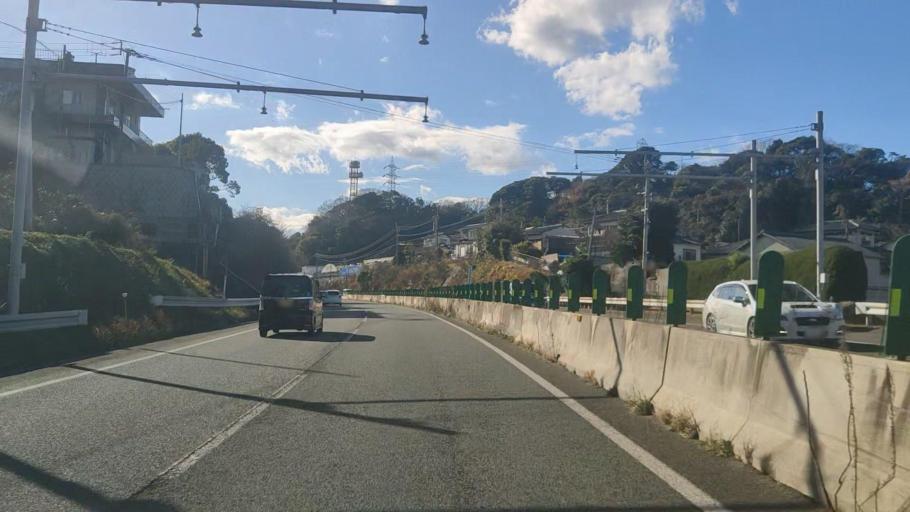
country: JP
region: Fukuoka
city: Kitakyushu
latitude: 33.8633
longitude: 130.8518
